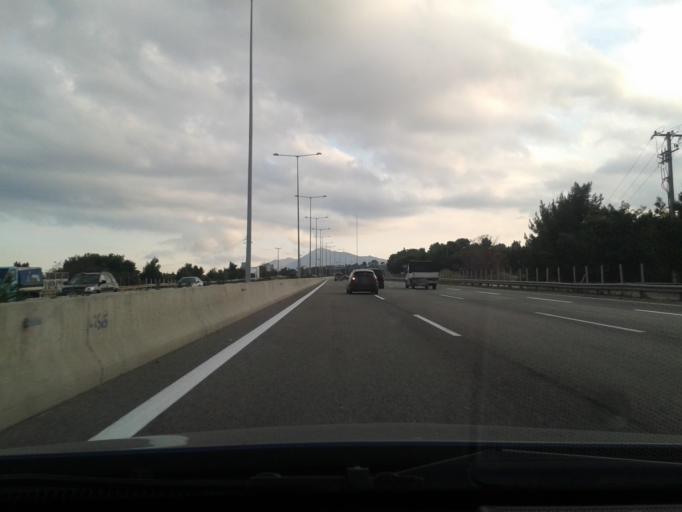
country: GR
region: Attica
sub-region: Nomarchia Anatolikis Attikis
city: Agios Stefanos
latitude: 38.1717
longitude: 23.8552
